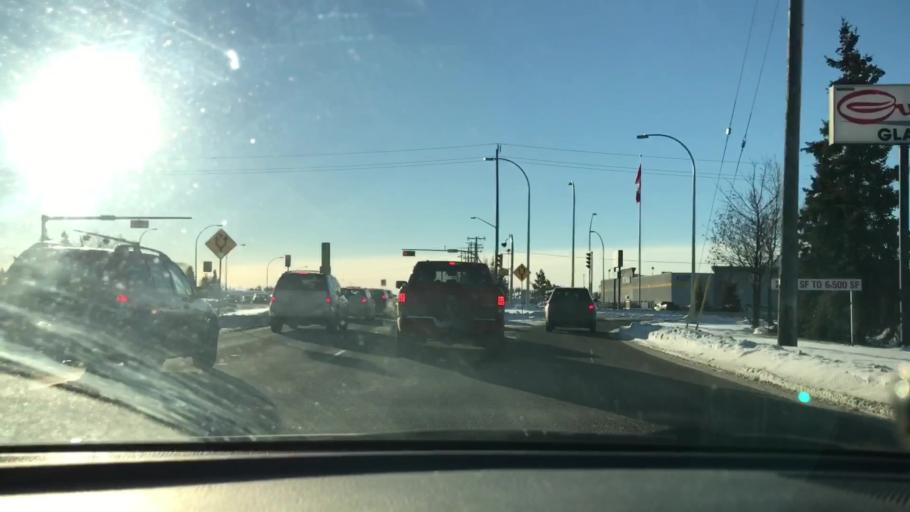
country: CA
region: Alberta
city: Edmonton
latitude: 53.4888
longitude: -113.4674
